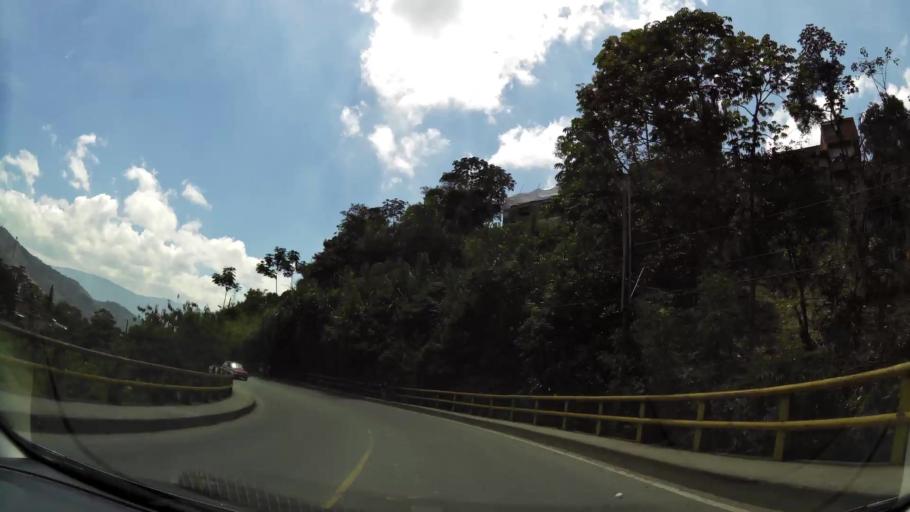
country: CO
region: Antioquia
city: La Estrella
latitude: 6.1823
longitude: -75.6558
